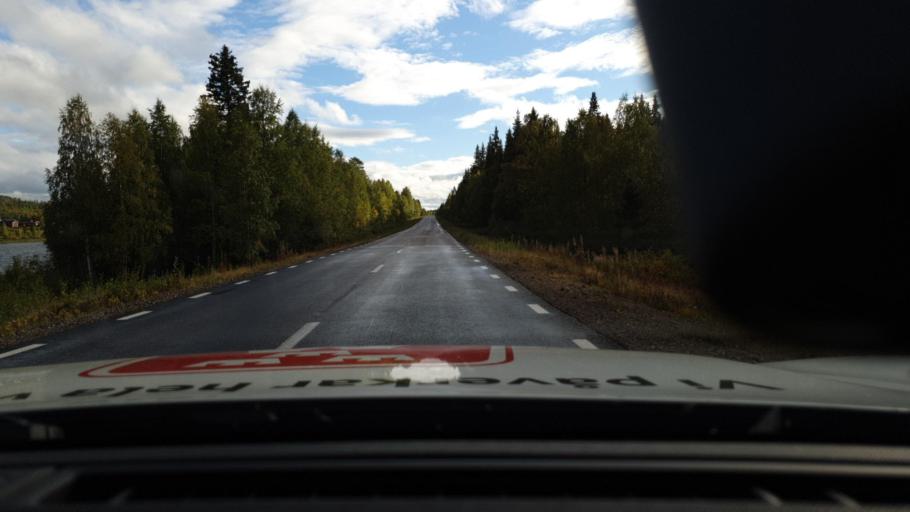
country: SE
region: Norrbotten
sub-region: Overkalix Kommun
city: OEverkalix
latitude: 66.8055
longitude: 22.7354
